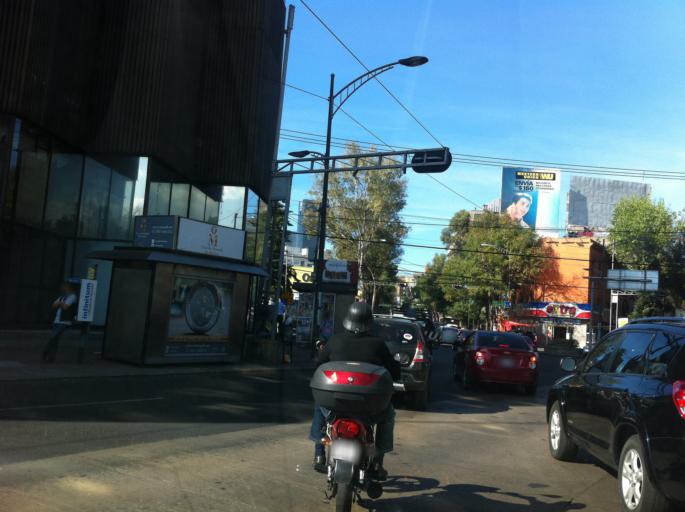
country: MX
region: Mexico City
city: Benito Juarez
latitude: 19.4185
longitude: -99.1645
